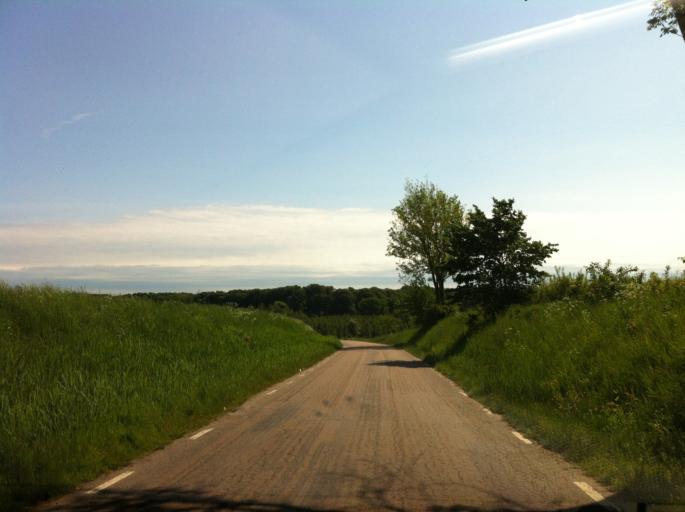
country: SE
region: Skane
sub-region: Helsingborg
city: Glumslov
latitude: 55.9630
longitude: 12.8757
